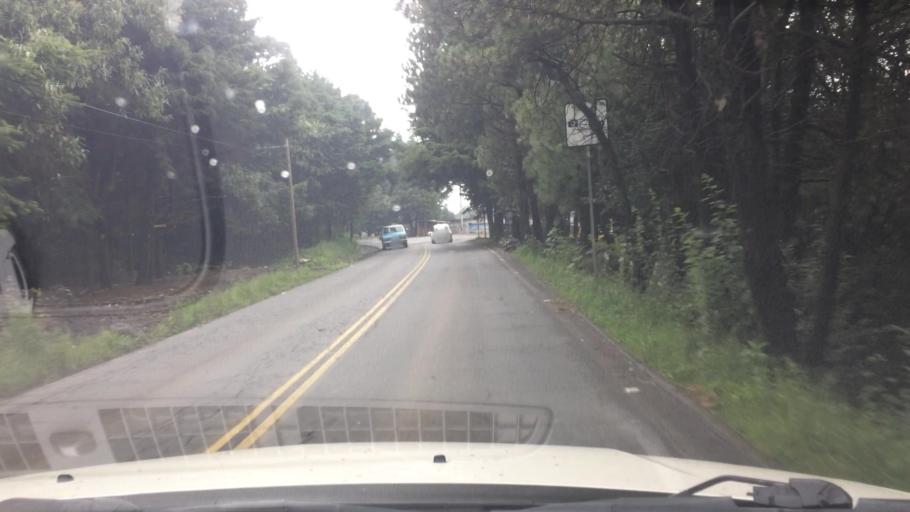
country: MX
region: Mexico City
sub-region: Tlalpan
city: Lomas de Tepemecatl
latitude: 19.2318
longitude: -99.2174
